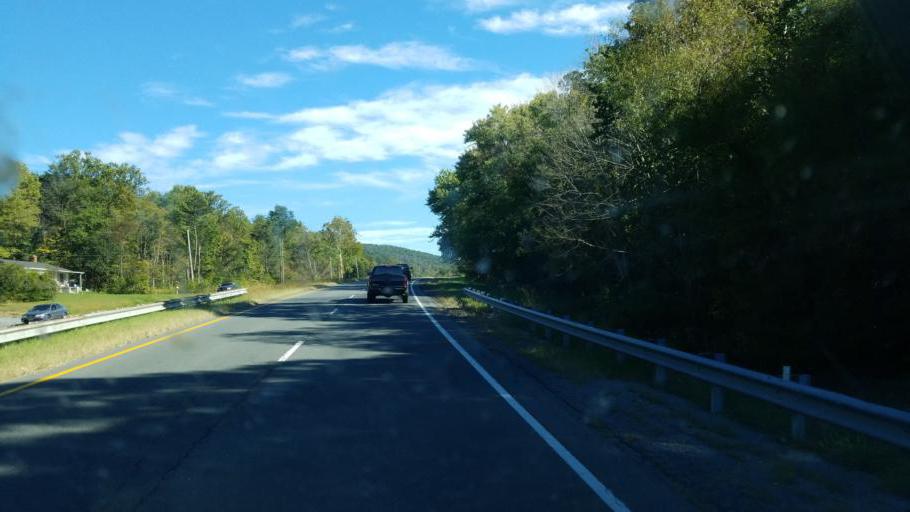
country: US
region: Virginia
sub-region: Warren County
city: Shenandoah Farms
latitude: 39.0329
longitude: -77.9875
